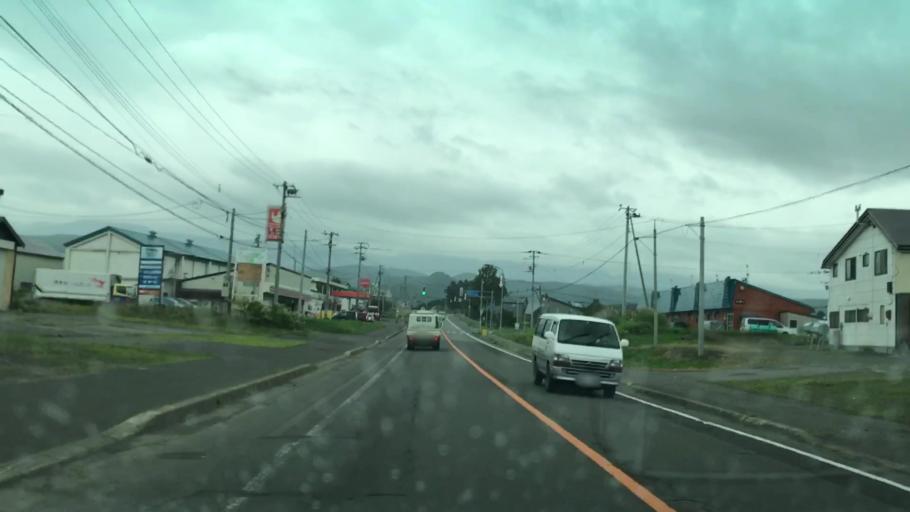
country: JP
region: Hokkaido
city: Niseko Town
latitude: 42.8105
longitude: 140.5416
